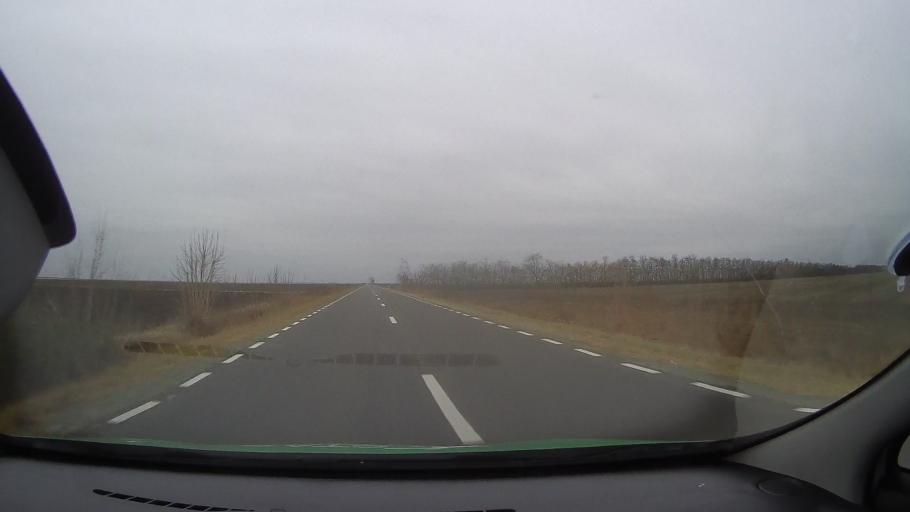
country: RO
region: Ialomita
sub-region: Comuna Gheorghe Lazar
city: Gheorghe Lazar
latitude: 44.6678
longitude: 27.4165
